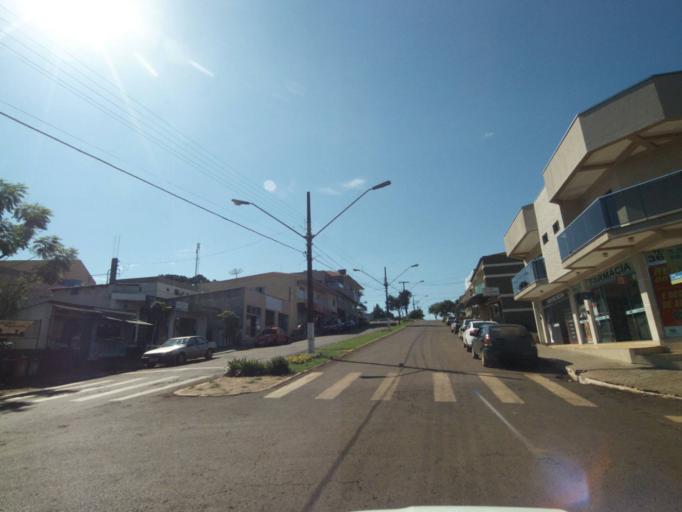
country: BR
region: Parana
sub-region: Laranjeiras Do Sul
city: Laranjeiras do Sul
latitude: -25.4898
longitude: -52.5274
